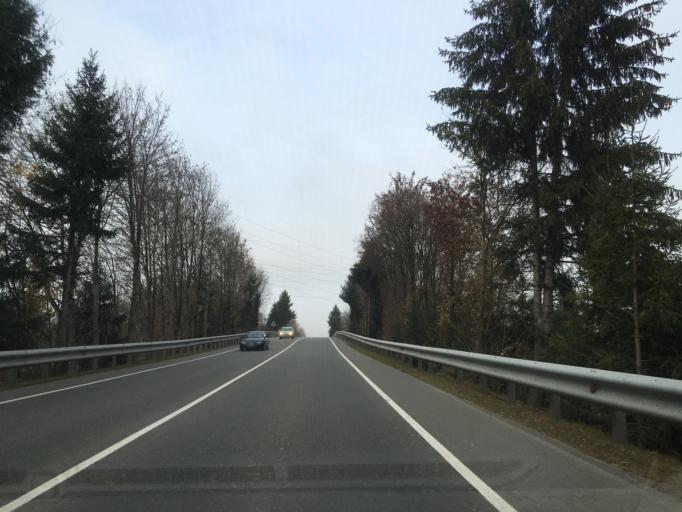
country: AT
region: Vorarlberg
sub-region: Politischer Bezirk Dornbirn
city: Hohenems
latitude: 47.3906
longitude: 9.6836
